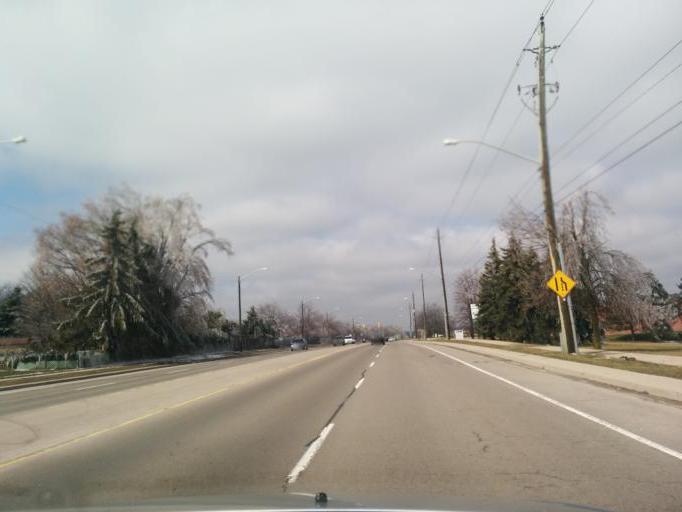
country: CA
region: Ontario
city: Waterloo
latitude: 43.4989
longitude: -80.5514
